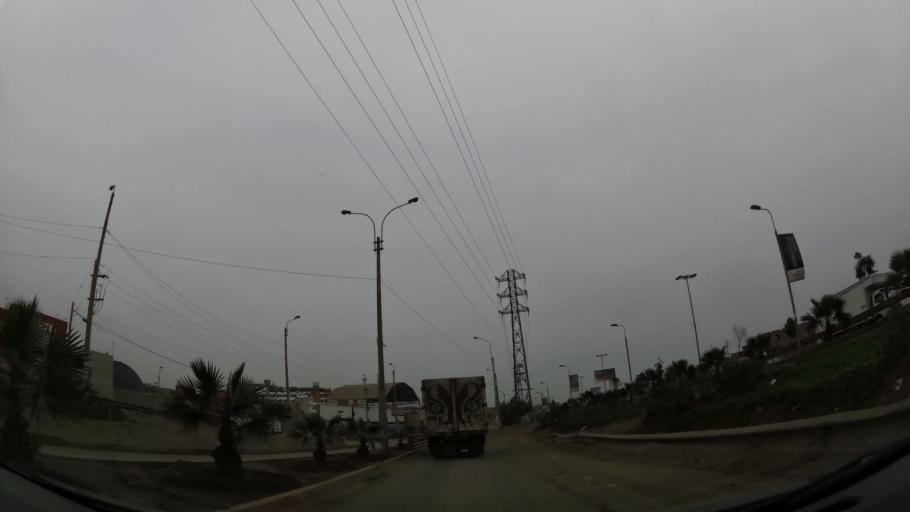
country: PE
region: Lima
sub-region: Lima
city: Surco
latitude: -12.1925
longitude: -76.9723
